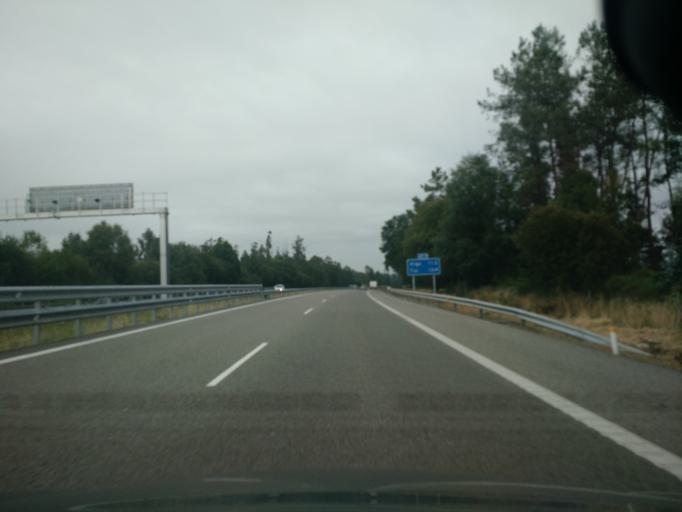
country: ES
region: Galicia
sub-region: Provincia da Coruna
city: Ordes
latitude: 43.0713
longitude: -8.3613
